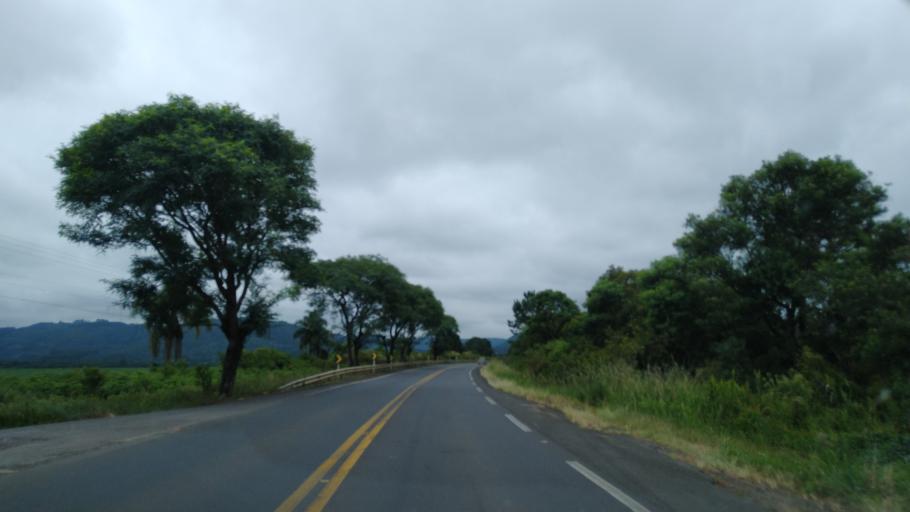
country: BR
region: Santa Catarina
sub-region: Porto Uniao
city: Porto Uniao
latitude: -26.2856
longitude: -51.0193
